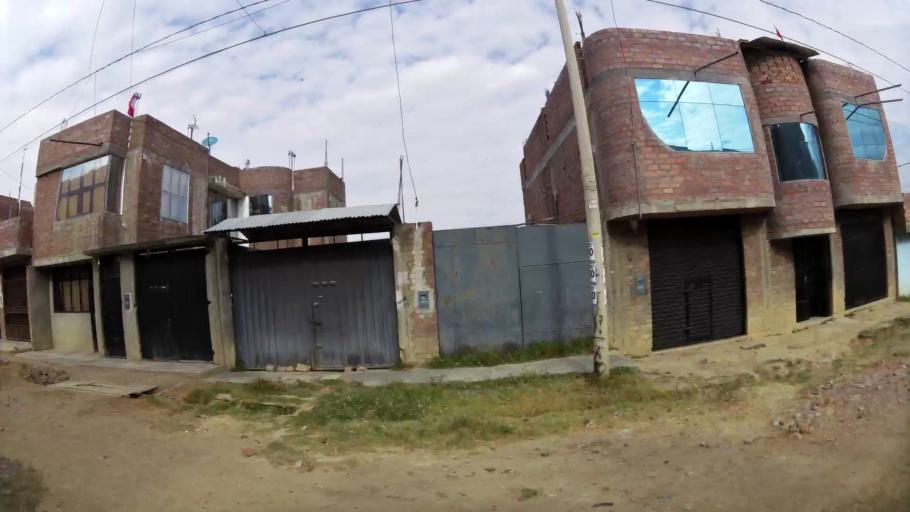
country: PE
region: Junin
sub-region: Provincia de Huancayo
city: Huancayo
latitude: -12.0524
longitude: -75.1877
